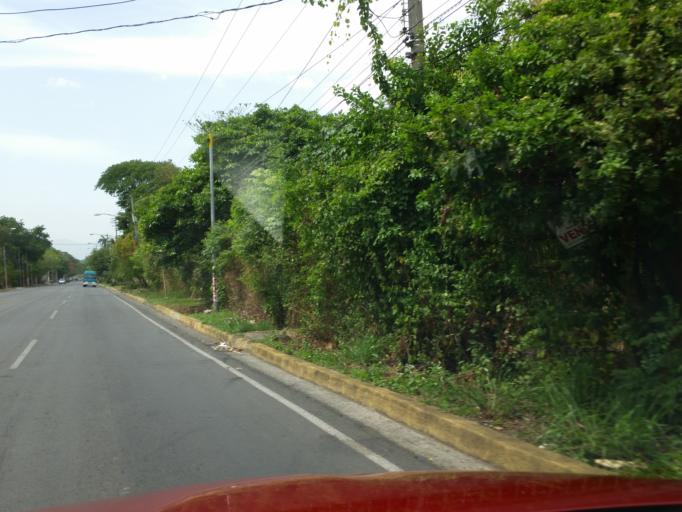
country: NI
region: Managua
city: Ciudad Sandino
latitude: 12.0773
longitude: -86.3239
